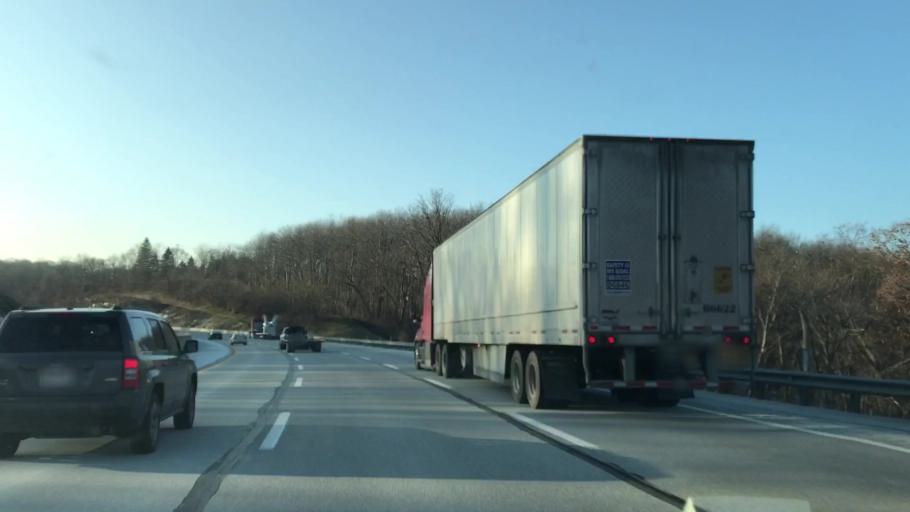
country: US
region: Pennsylvania
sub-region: Allegheny County
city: Gibsonia
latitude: 40.6441
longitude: -80.0163
